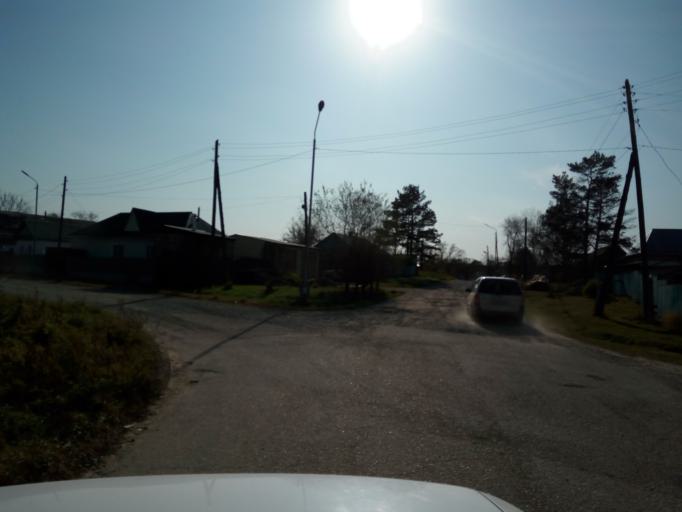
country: RU
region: Primorskiy
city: Dal'nerechensk
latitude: 45.9225
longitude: 133.7165
